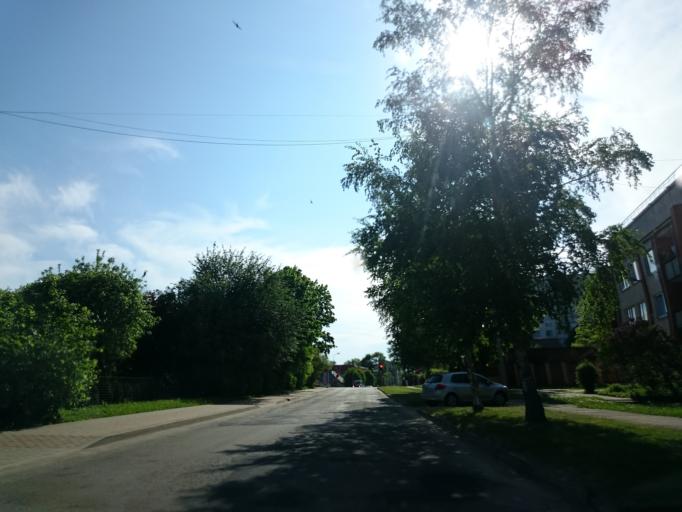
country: LV
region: Dobeles Rajons
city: Dobele
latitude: 56.6175
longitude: 23.2871
